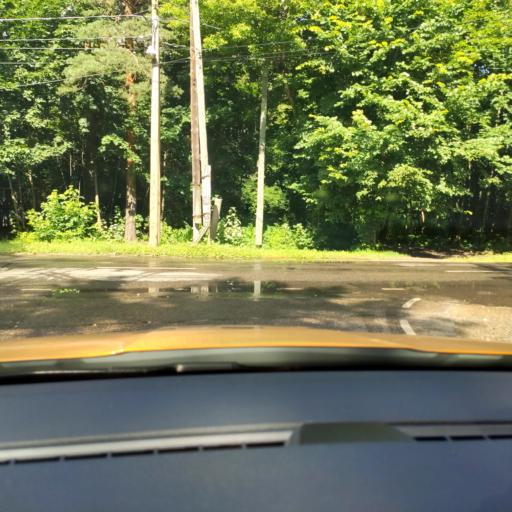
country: RU
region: Moscow
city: Zhulebino
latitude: 55.7016
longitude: 37.8755
